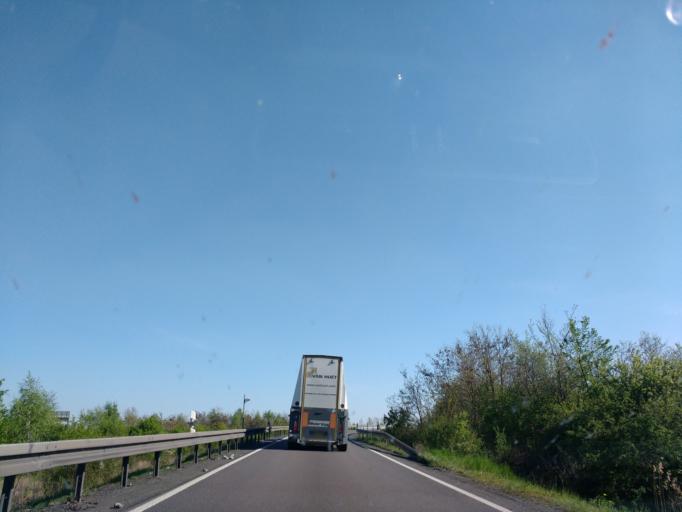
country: DE
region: Saxony
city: Wiedemar
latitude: 51.4291
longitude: 12.2012
